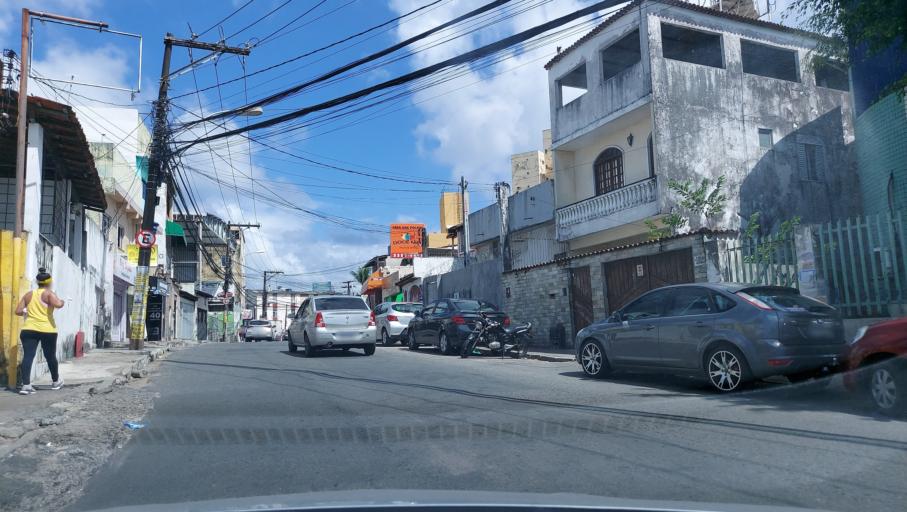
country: BR
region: Bahia
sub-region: Salvador
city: Salvador
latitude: -12.9855
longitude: -38.4772
